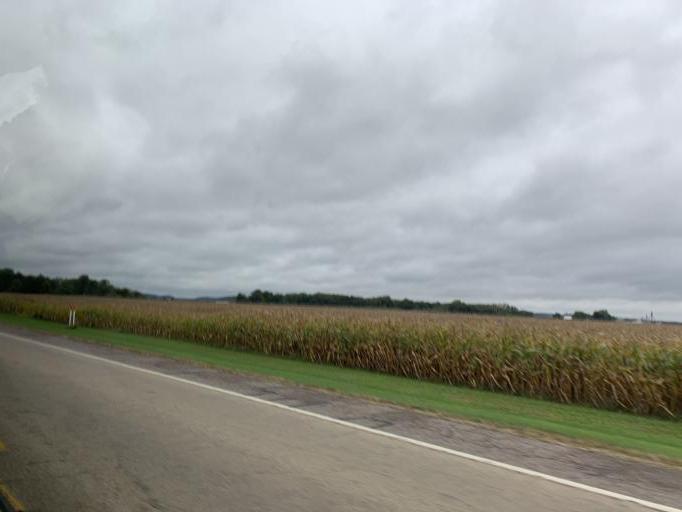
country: US
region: Wisconsin
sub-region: Sauk County
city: Prairie du Sac
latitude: 43.2710
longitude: -89.7901
